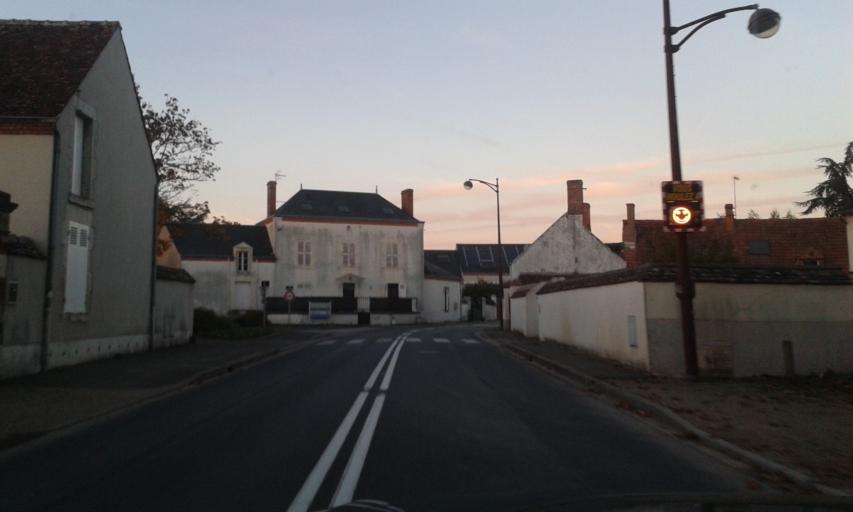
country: FR
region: Centre
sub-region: Departement du Loiret
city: Olivet
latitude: 47.8492
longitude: 1.8831
